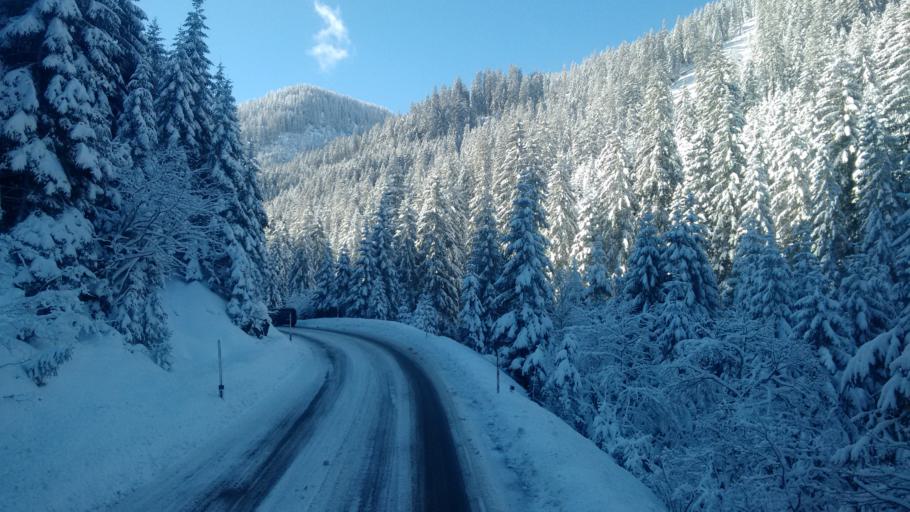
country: AT
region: Salzburg
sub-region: Politischer Bezirk Sankt Johann im Pongau
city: Untertauern
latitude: 47.3120
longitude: 13.4489
